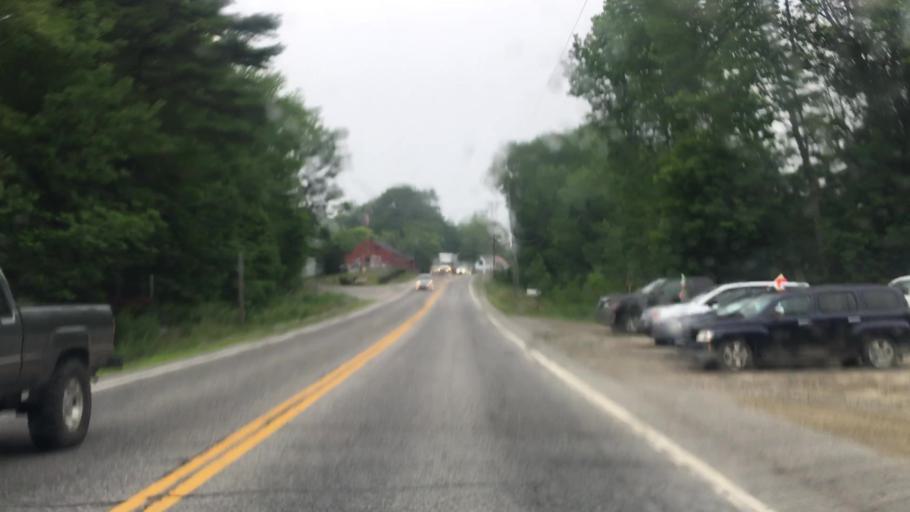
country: US
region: Maine
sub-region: Lincoln County
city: Edgecomb
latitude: 43.9559
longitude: -69.6294
